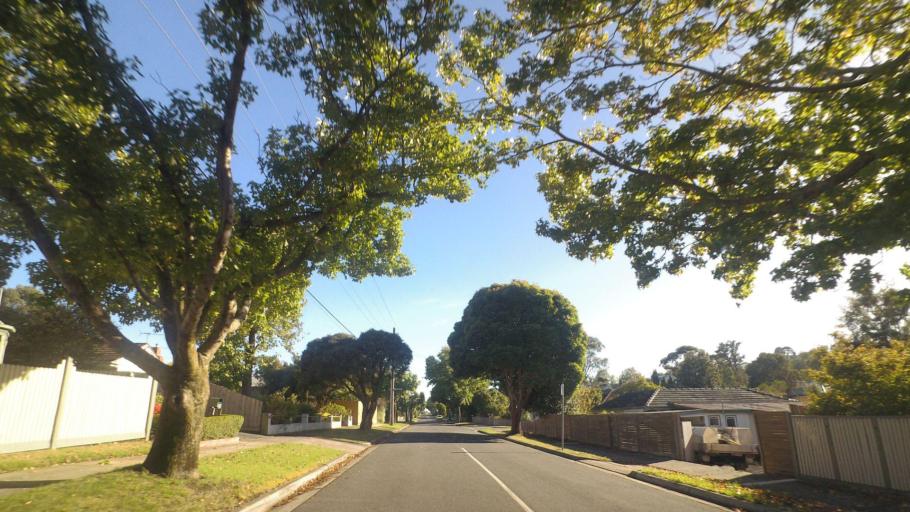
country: AU
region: Victoria
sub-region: Knox
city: Ferntree Gully
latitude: -37.8847
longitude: 145.2858
